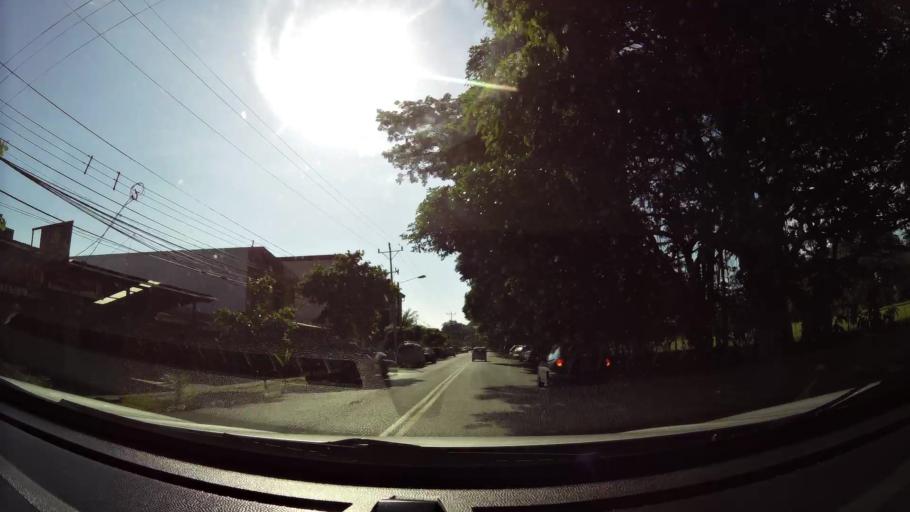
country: CR
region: Puntarenas
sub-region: Canton de Garabito
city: Jaco
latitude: 9.6117
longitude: -84.6179
